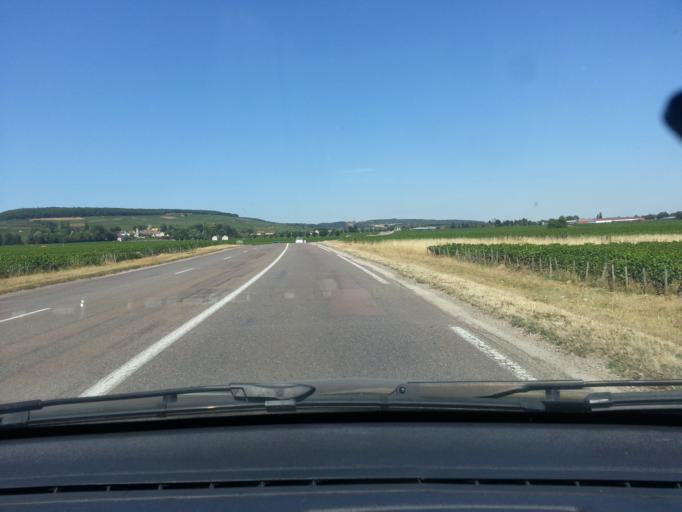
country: FR
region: Bourgogne
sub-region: Departement de la Cote-d'Or
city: Beaune
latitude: 47.0539
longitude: 4.8581
